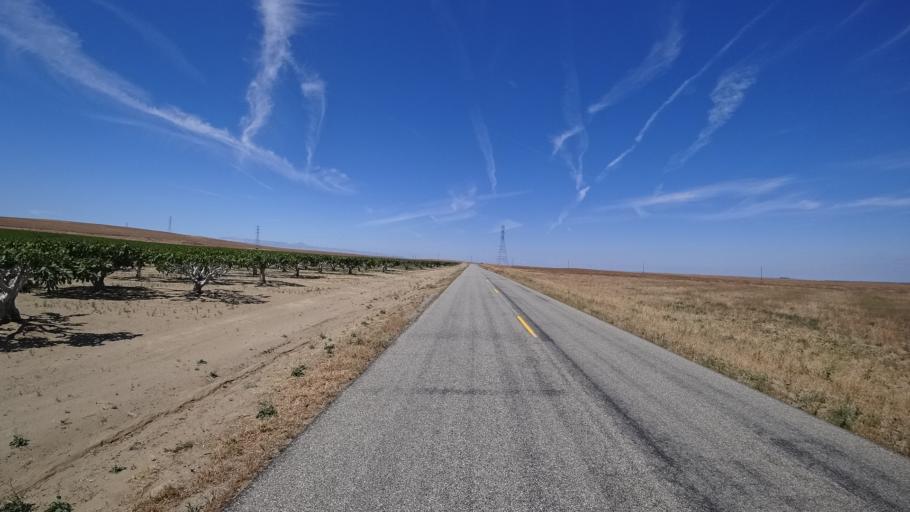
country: US
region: California
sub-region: Kings County
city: Kettleman City
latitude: 35.7848
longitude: -119.8823
